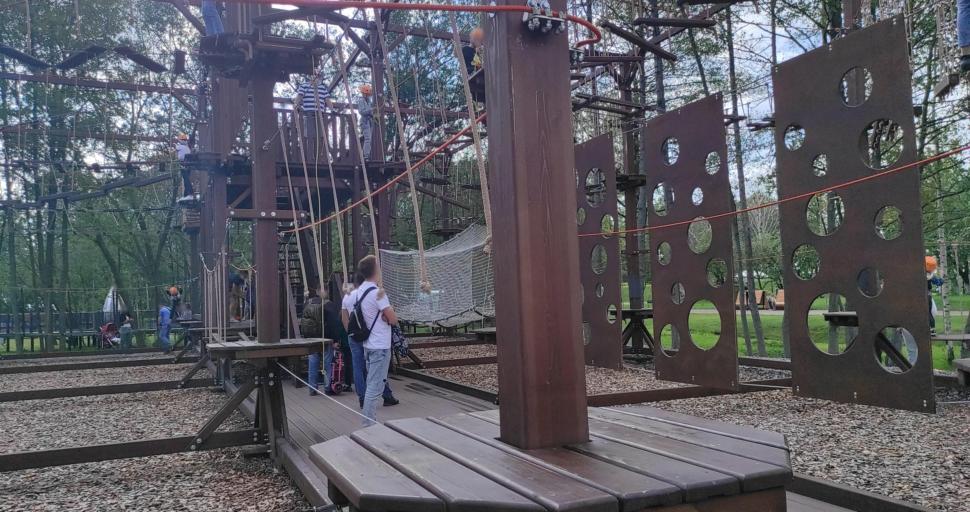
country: RU
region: St.-Petersburg
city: Kronshtadt
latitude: 59.9946
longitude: 29.7448
